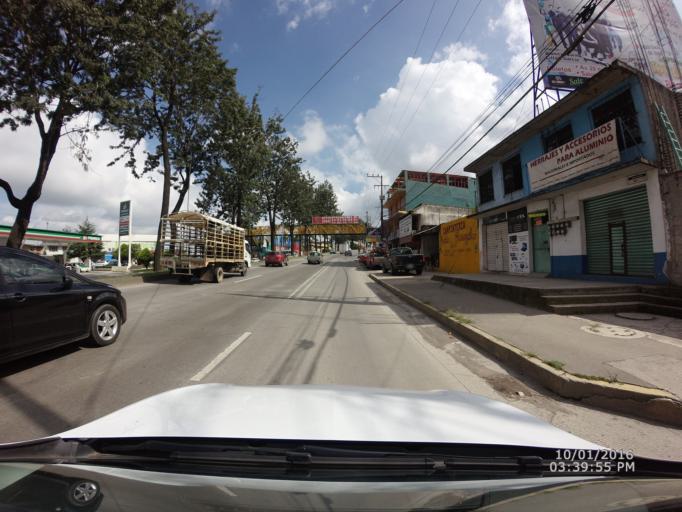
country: MX
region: Veracruz
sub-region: Xalapa
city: Xalapa de Enriquez
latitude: 19.5569
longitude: -96.9159
